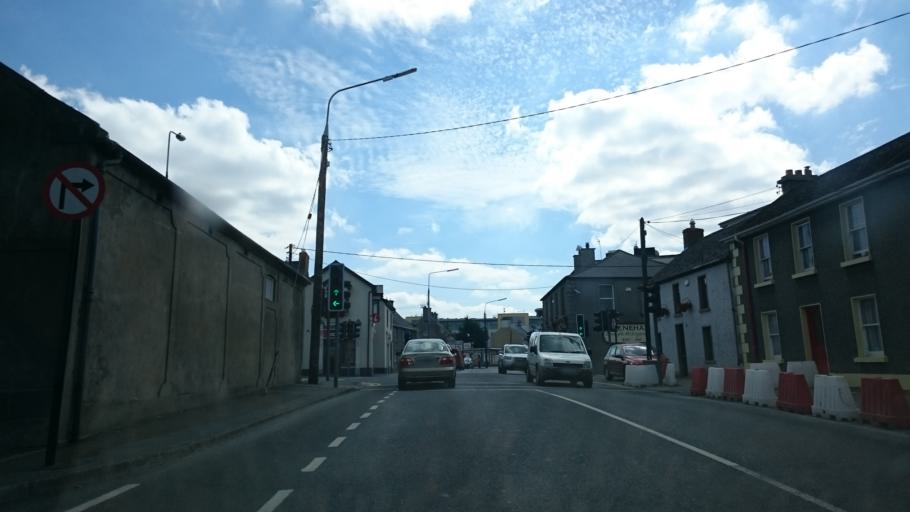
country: IE
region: Leinster
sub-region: Kilkenny
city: Kilkenny
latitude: 52.6575
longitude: -7.2463
